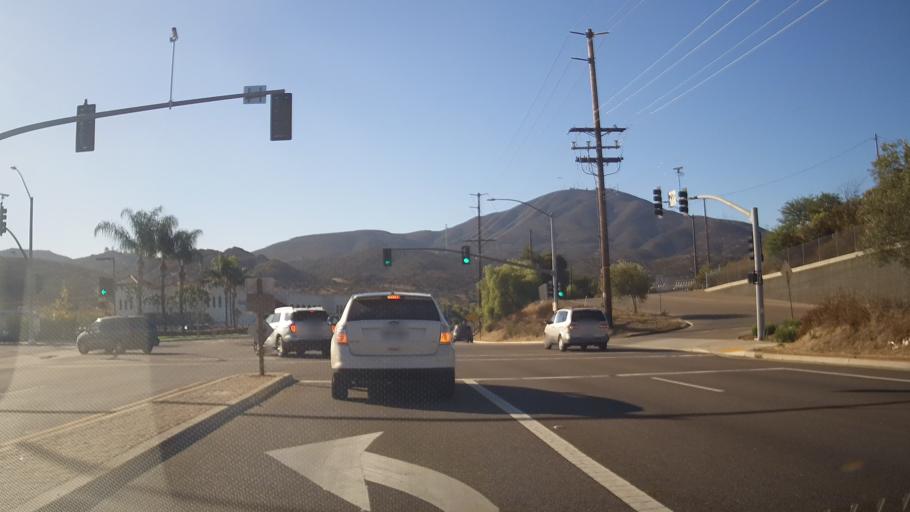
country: US
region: California
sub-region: San Diego County
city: Rancho San Diego
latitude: 32.7374
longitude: -116.9415
